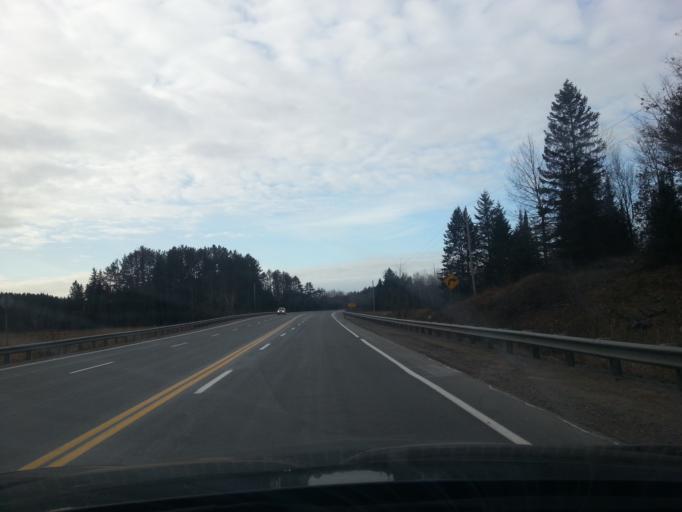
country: CA
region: Ontario
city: Belleville
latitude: 44.5361
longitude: -77.3809
